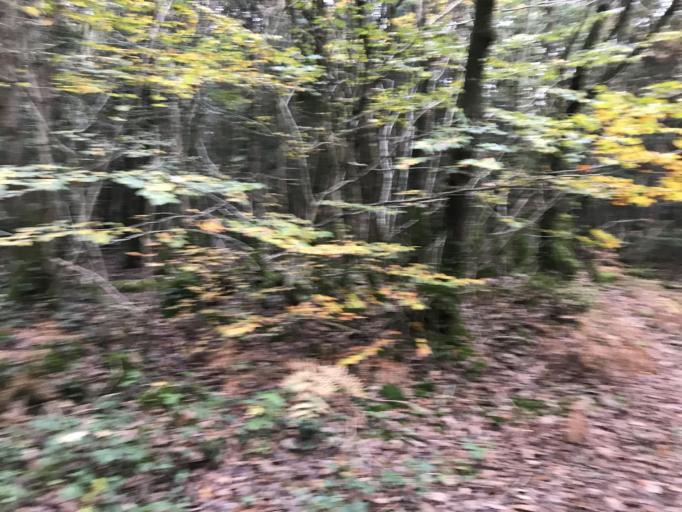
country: FR
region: Brittany
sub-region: Departement du Finistere
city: Hopital-Camfrout
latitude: 48.3336
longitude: -4.2192
